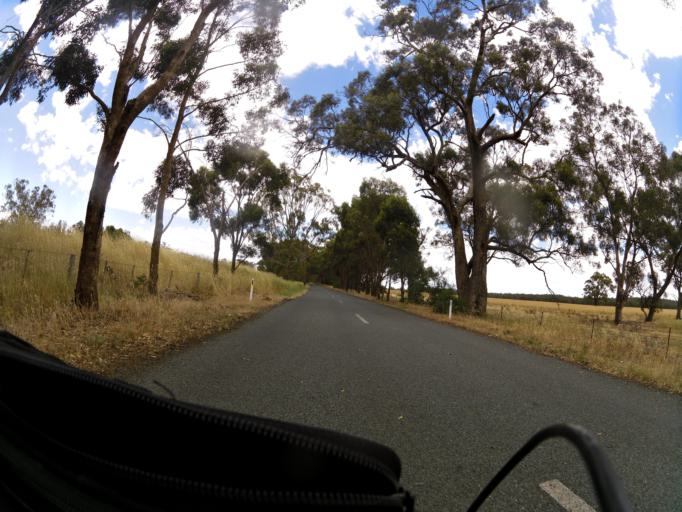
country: AU
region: Victoria
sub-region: Greater Shepparton
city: Shepparton
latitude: -36.6520
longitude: 145.2047
